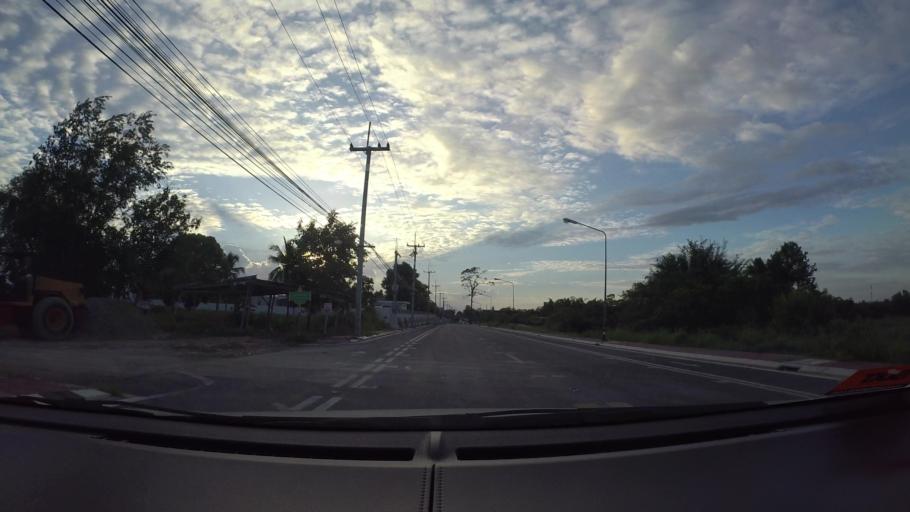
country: TH
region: Chon Buri
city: Sattahip
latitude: 12.7771
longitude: 100.9437
